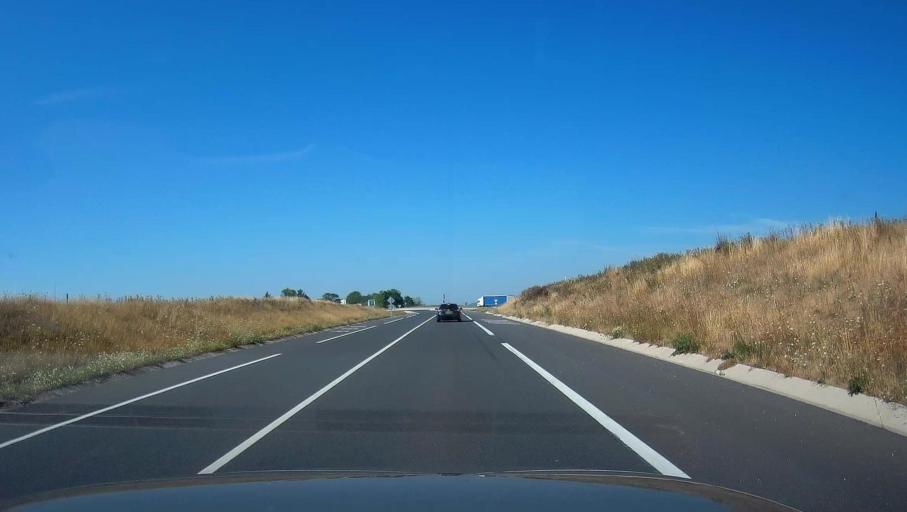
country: FR
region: Lorraine
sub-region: Departement de Meurthe-et-Moselle
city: Colombey-les-Belles
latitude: 48.5462
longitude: 5.9114
